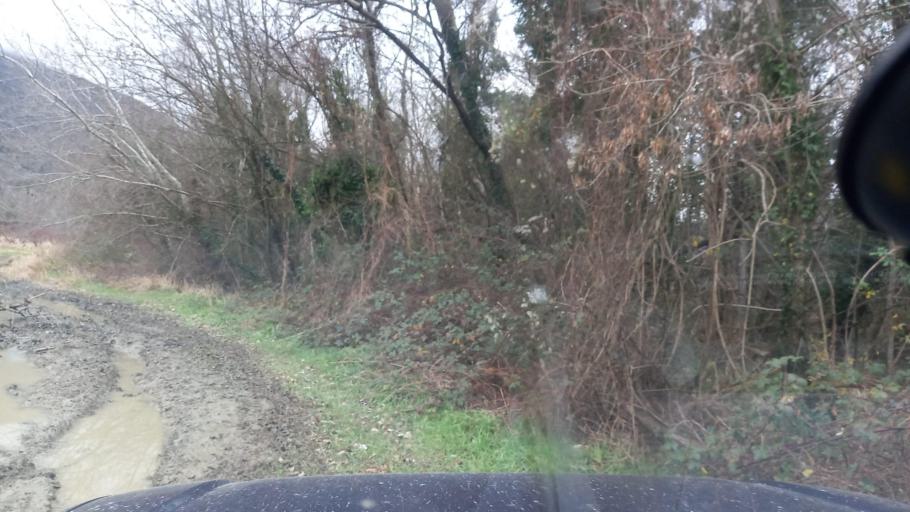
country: RU
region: Krasnodarskiy
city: Pshada
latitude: 44.5034
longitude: 38.4239
